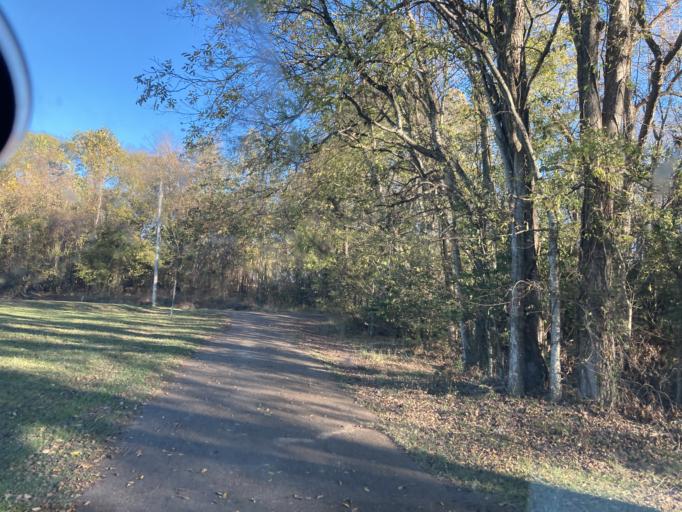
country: US
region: Mississippi
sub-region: Yazoo County
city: Yazoo City
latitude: 32.8509
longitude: -90.3983
